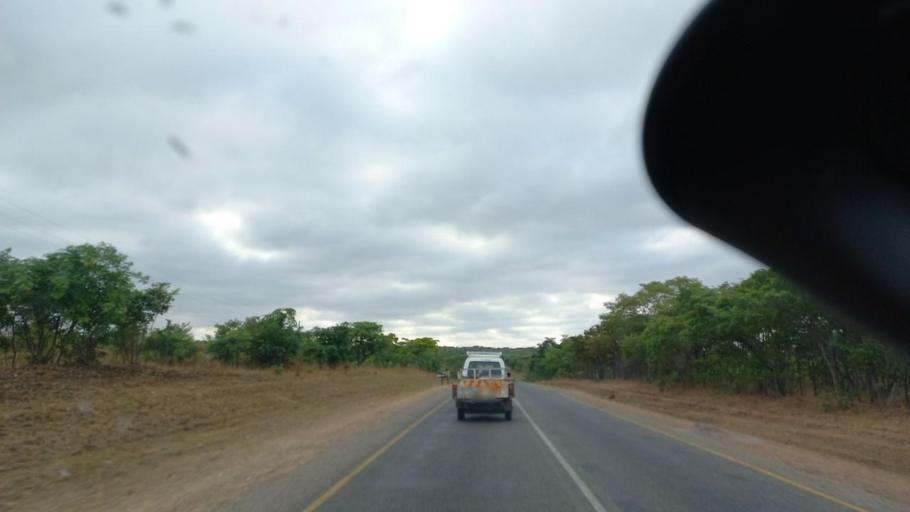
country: ZM
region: Lusaka
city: Chongwe
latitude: -15.2799
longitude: 28.7375
